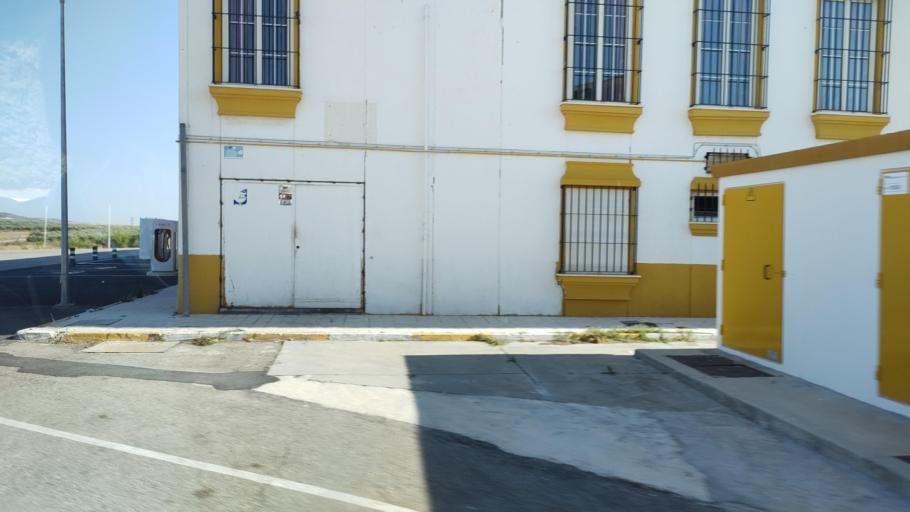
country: ES
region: Andalusia
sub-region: Provincia de Sevilla
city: Aguadulce
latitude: 37.2565
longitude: -4.9860
